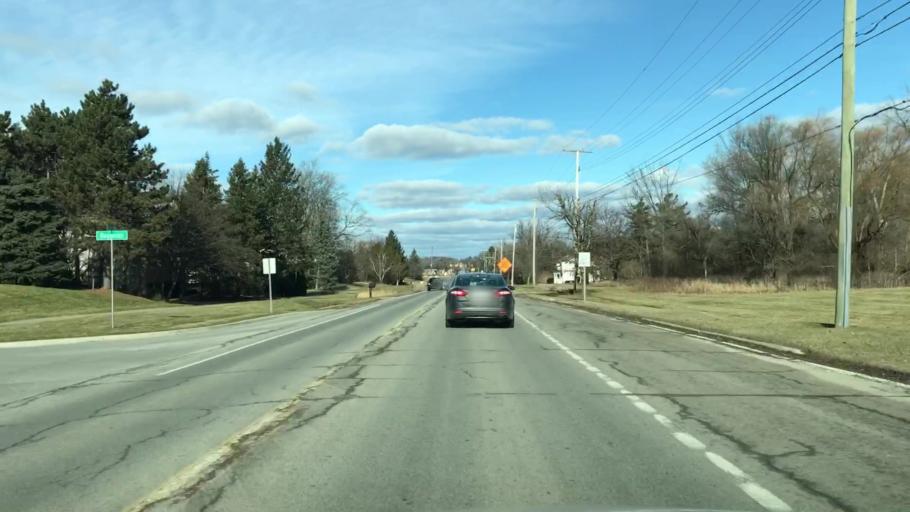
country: US
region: Michigan
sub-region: Oakland County
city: Auburn Hills
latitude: 42.6902
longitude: -83.1944
